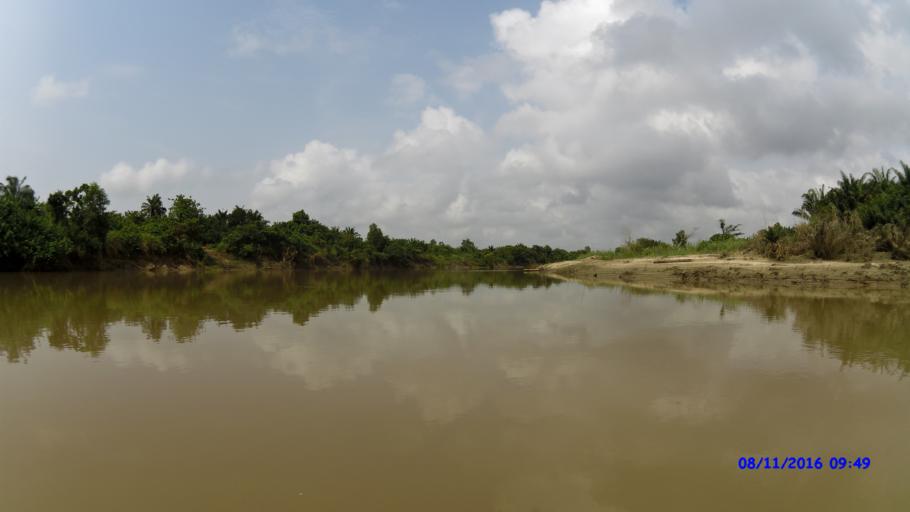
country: BJ
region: Mono
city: Come
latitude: 6.4306
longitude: 1.7689
